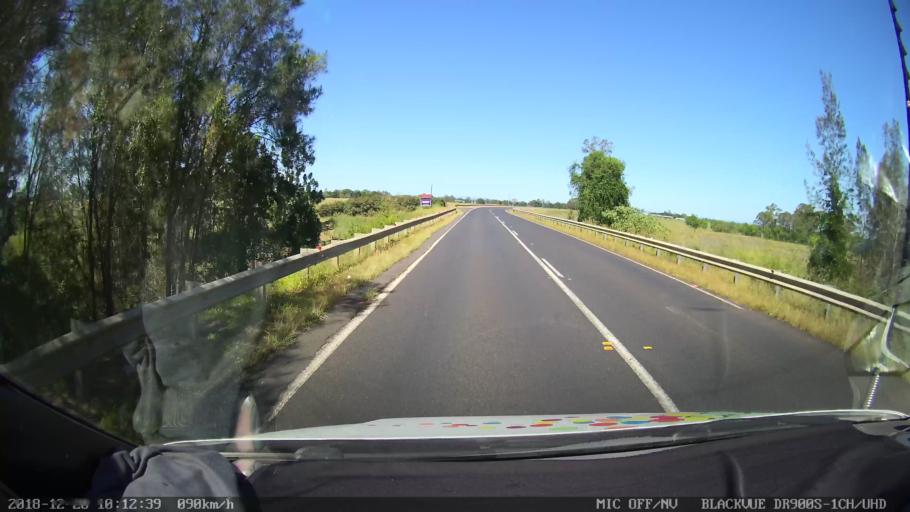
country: AU
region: New South Wales
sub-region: Richmond Valley
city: Casino
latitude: -28.8743
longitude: 153.1411
